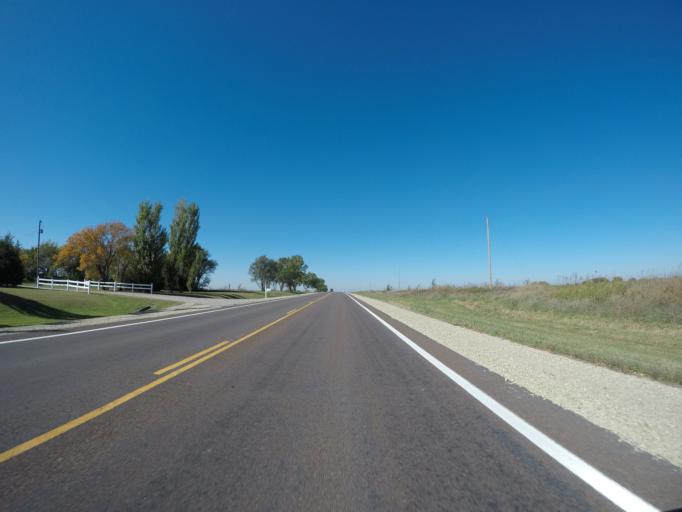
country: US
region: Kansas
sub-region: Riley County
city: Fort Riley North
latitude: 39.3067
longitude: -96.9095
